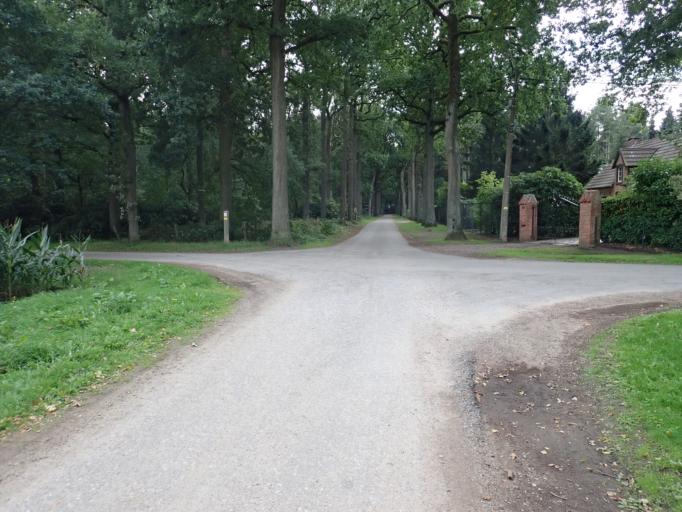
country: BE
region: Flanders
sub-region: Provincie Antwerpen
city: Kalmthout
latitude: 51.3552
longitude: 4.5179
